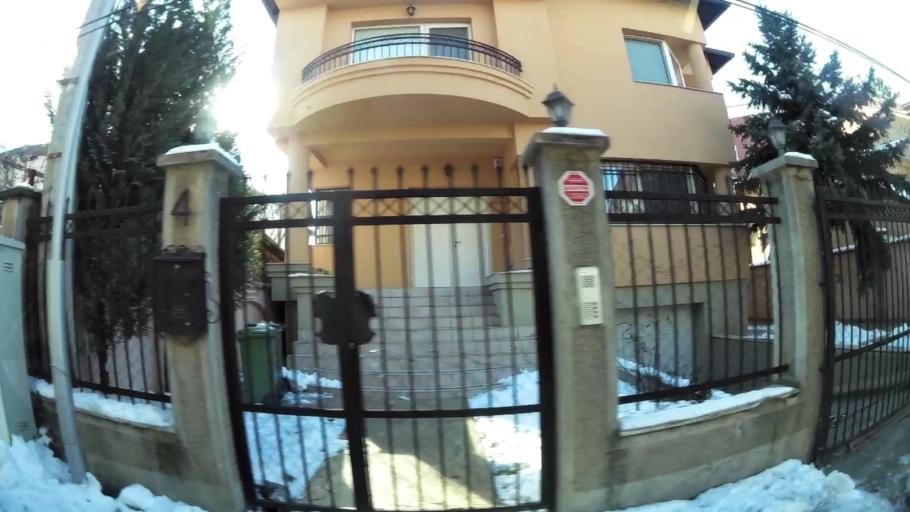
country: MK
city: Krushopek
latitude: 42.0076
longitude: 21.3777
